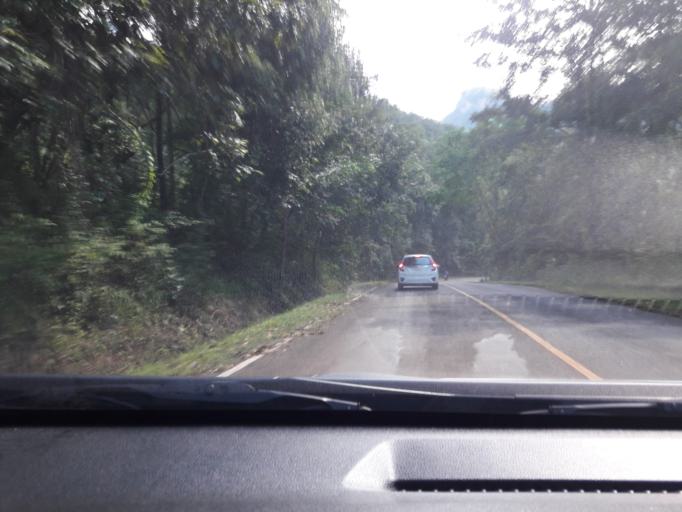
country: TH
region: Mae Hong Son
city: Sop Pong
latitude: 19.5643
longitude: 98.1961
